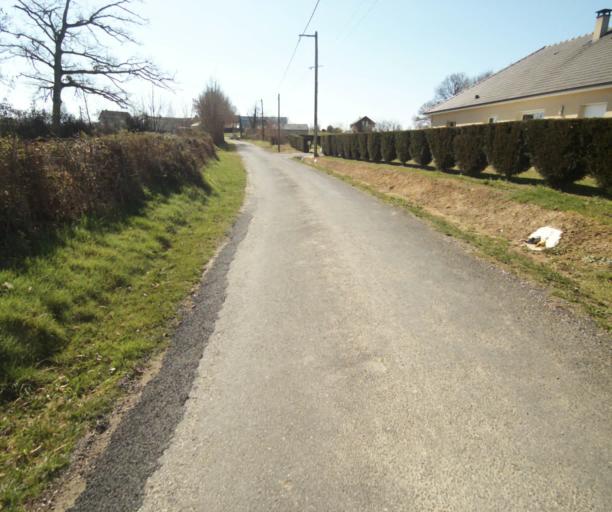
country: FR
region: Limousin
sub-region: Departement de la Correze
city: Saint-Mexant
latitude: 45.3093
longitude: 1.6012
